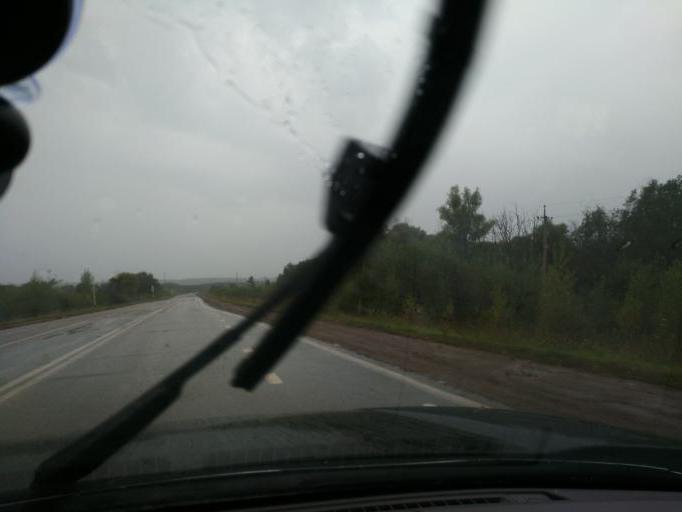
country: RU
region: Perm
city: Barda
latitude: 56.9439
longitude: 55.6145
